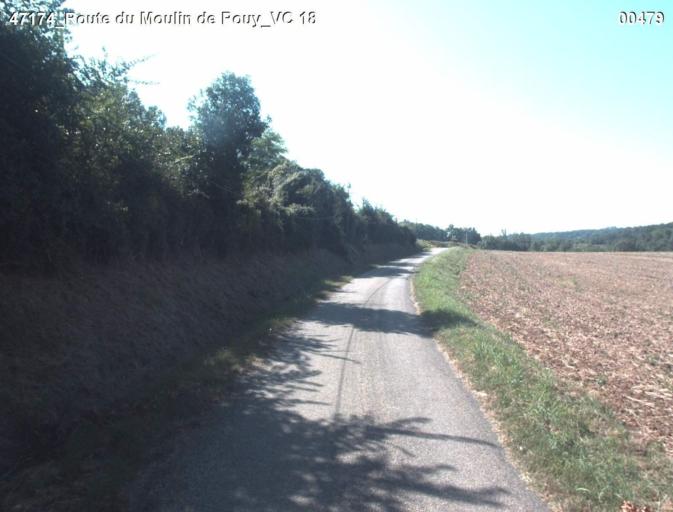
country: FR
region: Aquitaine
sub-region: Departement du Lot-et-Garonne
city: Mezin
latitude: 44.0598
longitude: 0.3195
